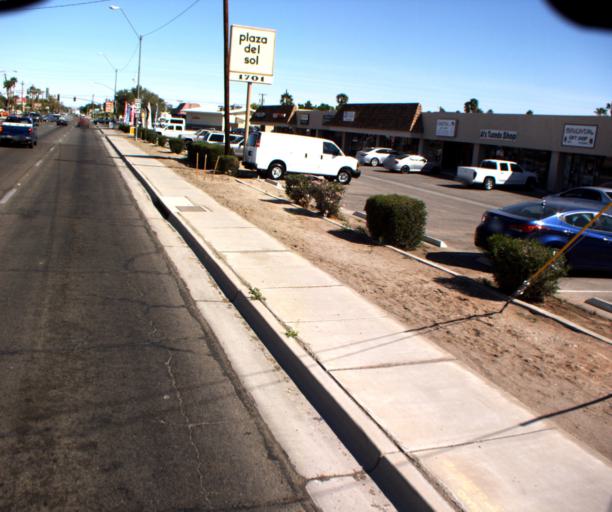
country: US
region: Arizona
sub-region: Yuma County
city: Yuma
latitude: 32.6970
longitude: -114.6504
